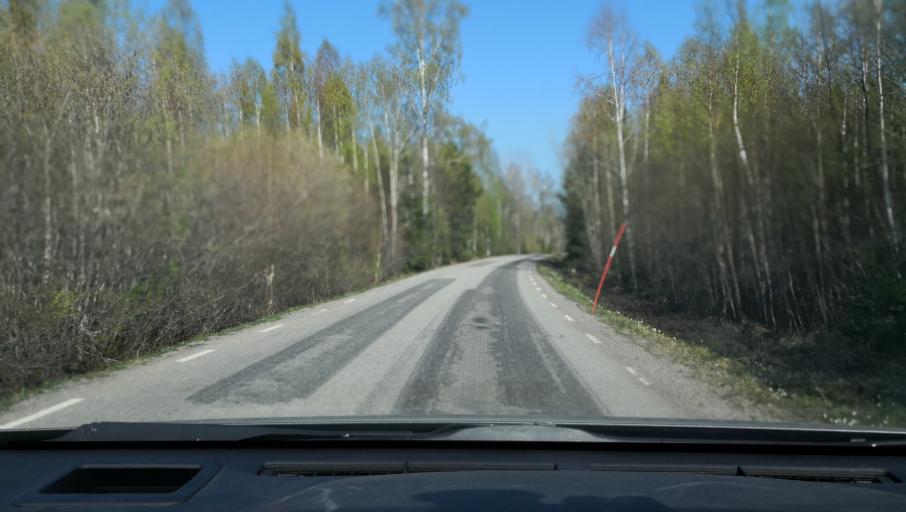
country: SE
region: Uppsala
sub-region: Heby Kommun
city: Heby
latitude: 60.0433
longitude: 16.8393
